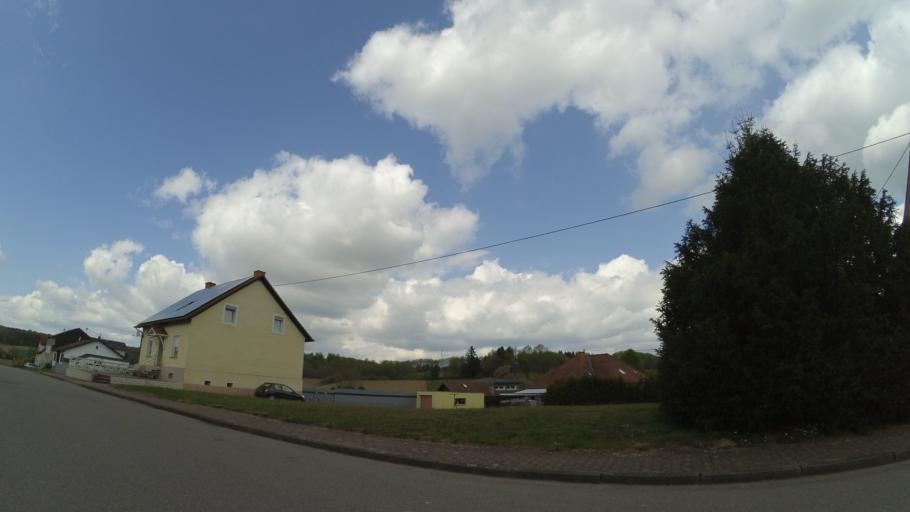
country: DE
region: Saarland
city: Wadern
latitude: 49.5066
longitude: 6.8623
